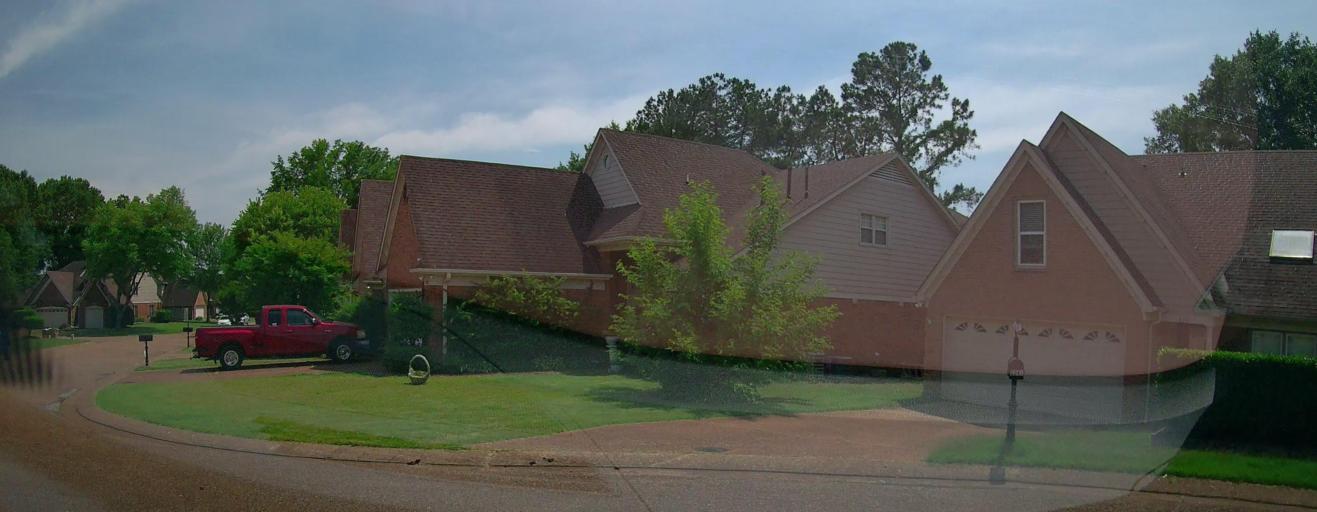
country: US
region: Tennessee
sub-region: Shelby County
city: Germantown
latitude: 35.0416
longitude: -89.7866
